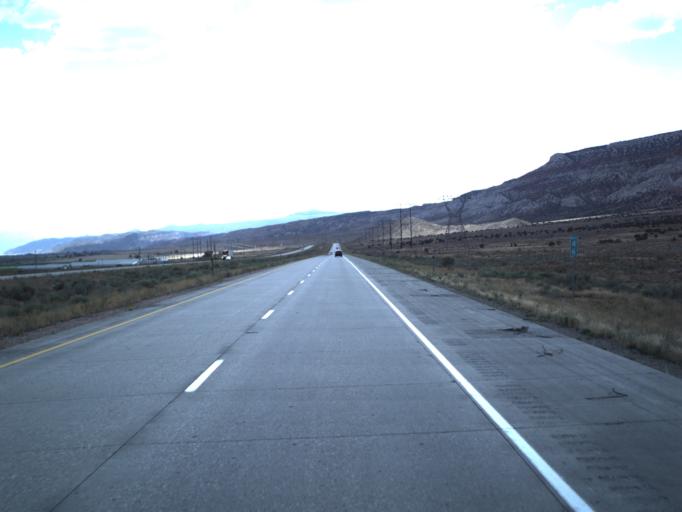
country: US
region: Utah
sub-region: Sevier County
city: Aurora
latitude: 38.8481
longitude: -112.0078
